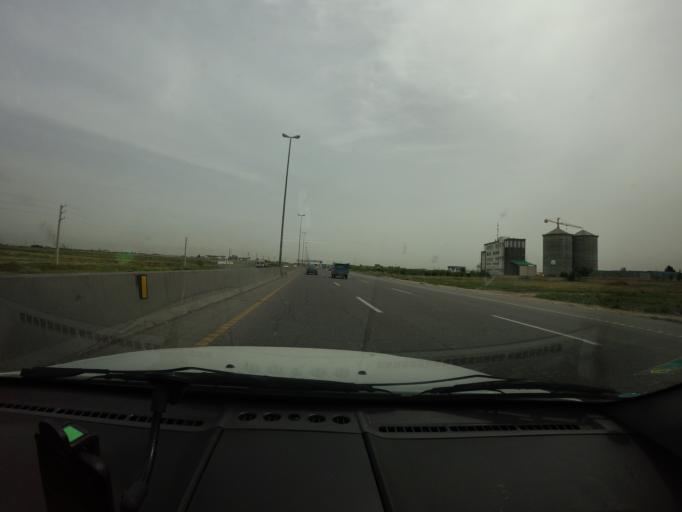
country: IR
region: Tehran
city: Robat Karim
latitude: 35.5313
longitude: 51.0940
